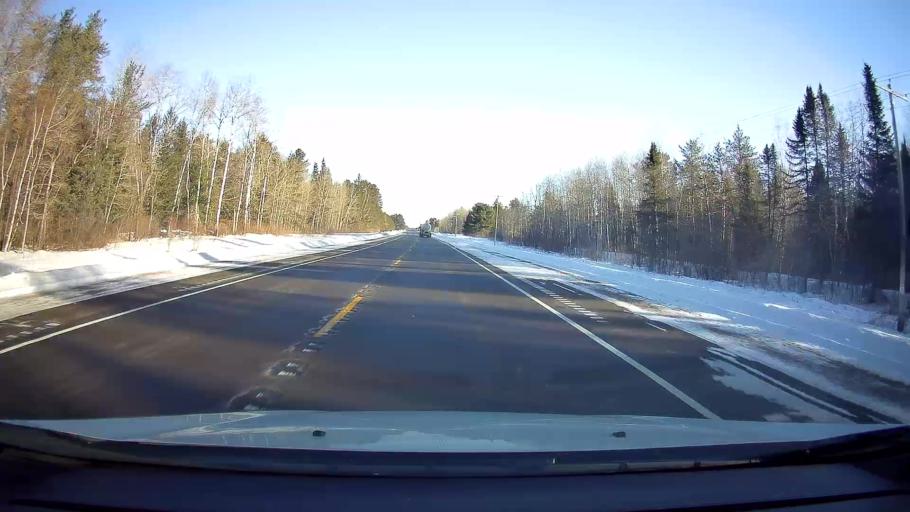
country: US
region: Wisconsin
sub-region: Sawyer County
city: Hayward
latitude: 46.0936
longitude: -91.3872
